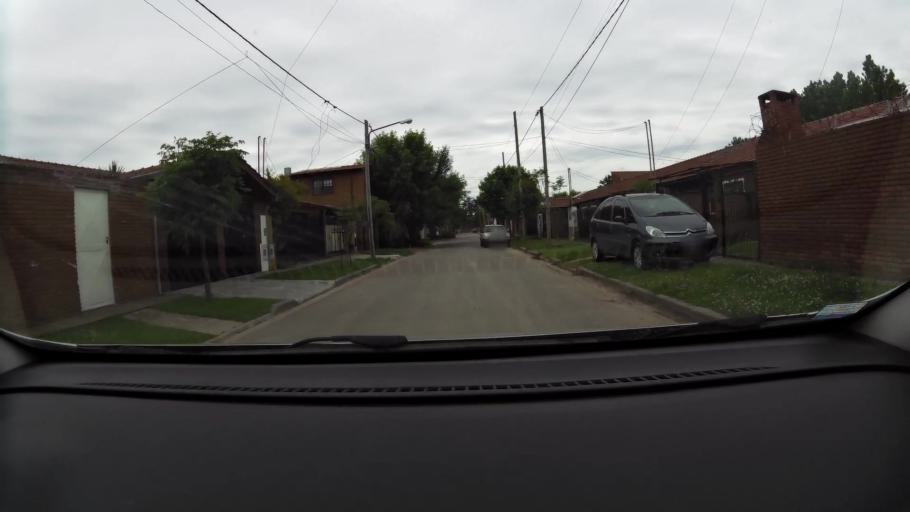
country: AR
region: Buenos Aires
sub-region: Partido de Campana
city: Campana
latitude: -34.1932
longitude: -58.9470
